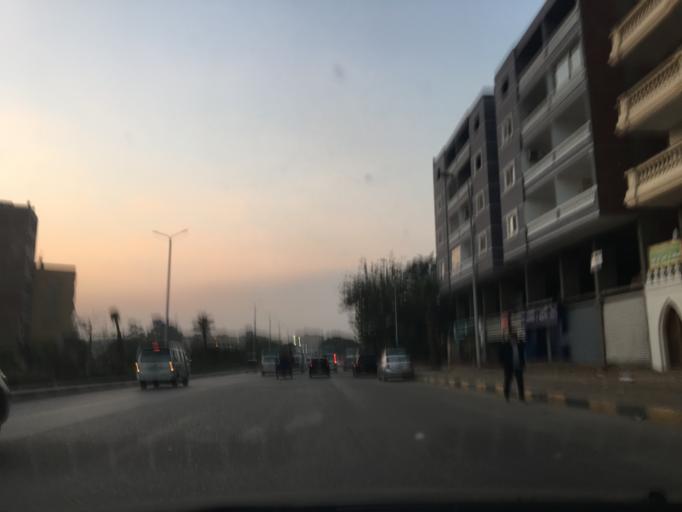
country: EG
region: Al Jizah
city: Al Jizah
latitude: 29.9897
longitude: 31.1362
